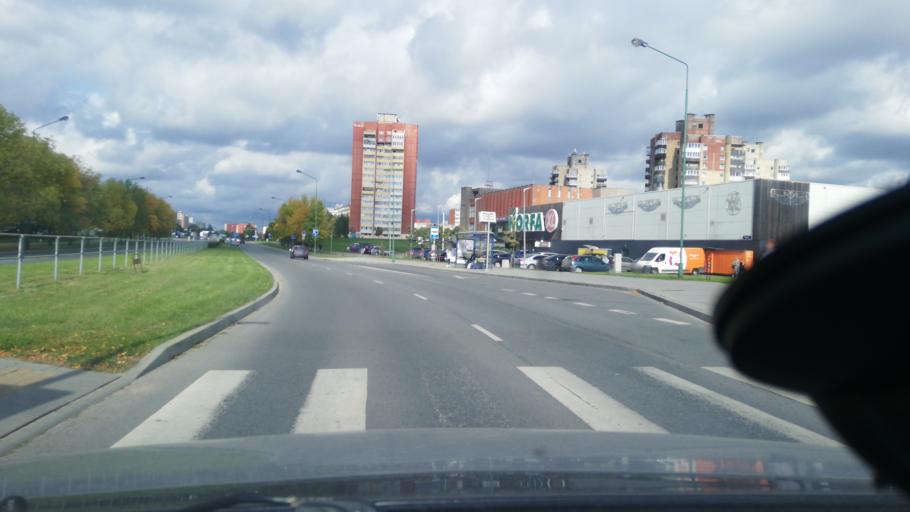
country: LT
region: Klaipedos apskritis
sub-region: Klaipeda
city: Klaipeda
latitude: 55.6674
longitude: 21.1954
